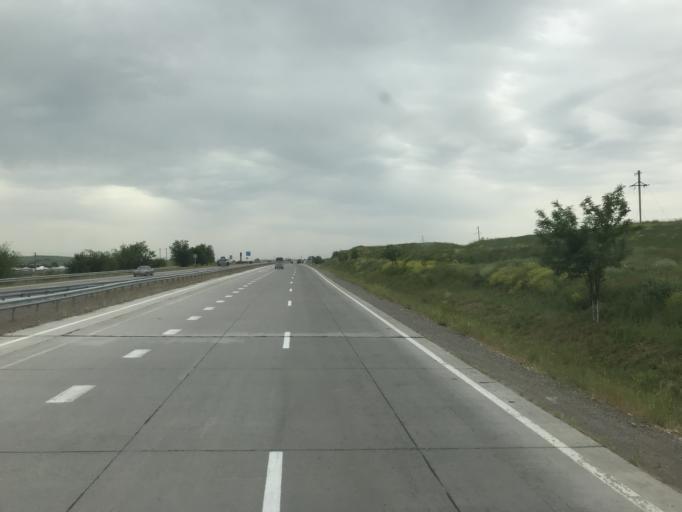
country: KZ
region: Ongtustik Qazaqstan
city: Qazyqurt
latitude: 41.8444
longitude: 69.4060
